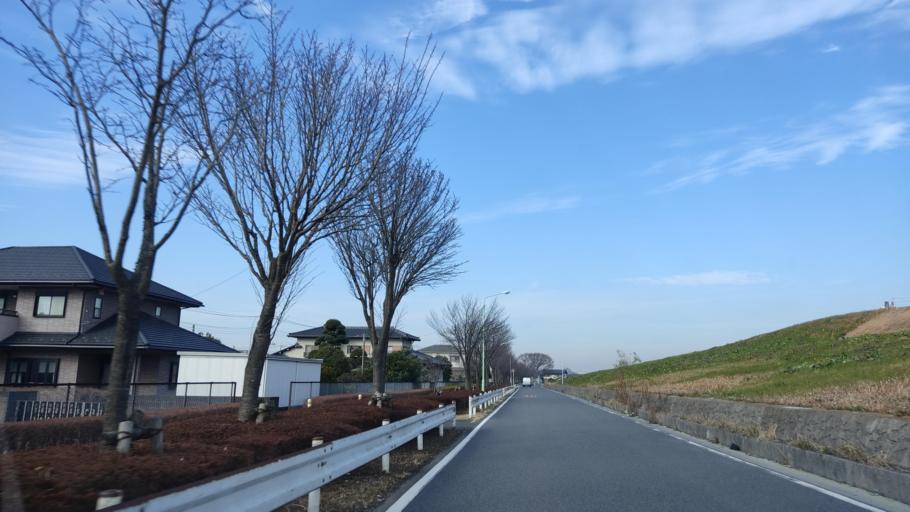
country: JP
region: Chiba
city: Matsudo
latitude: 35.8202
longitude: 139.8871
